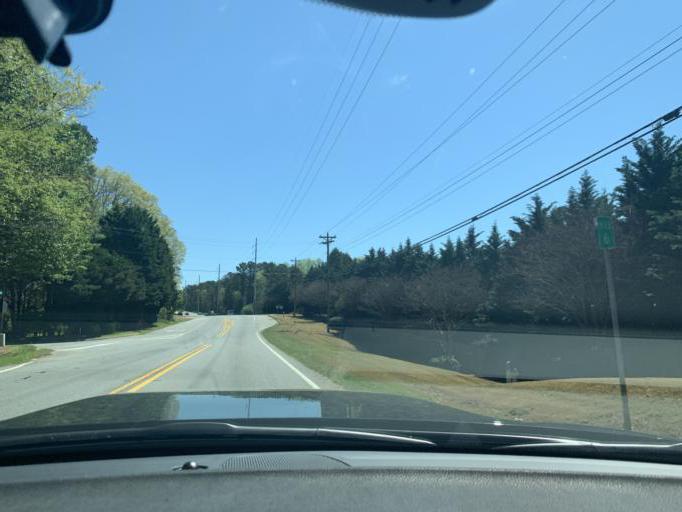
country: US
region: Georgia
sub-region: Forsyth County
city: Cumming
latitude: 34.1598
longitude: -84.1904
